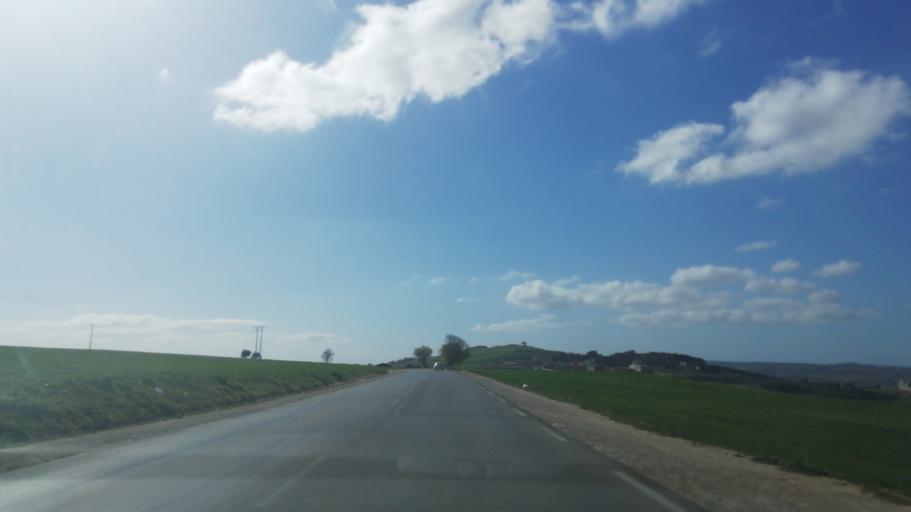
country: DZ
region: Relizane
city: Relizane
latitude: 36.0918
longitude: 0.4469
